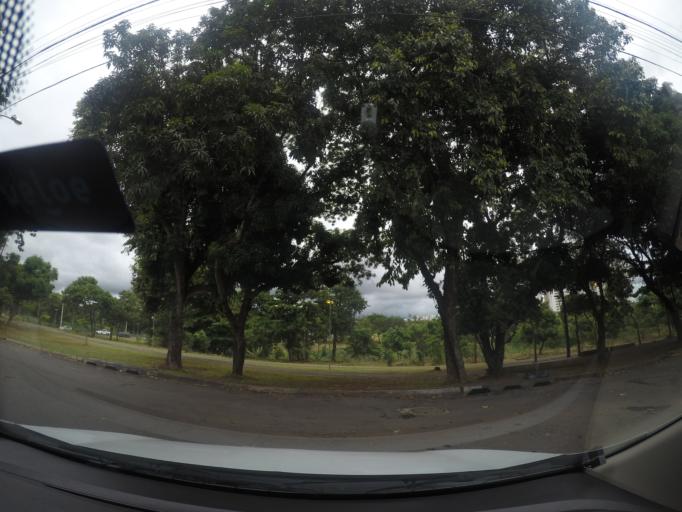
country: BR
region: Goias
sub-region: Goiania
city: Goiania
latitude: -16.7155
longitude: -49.3203
